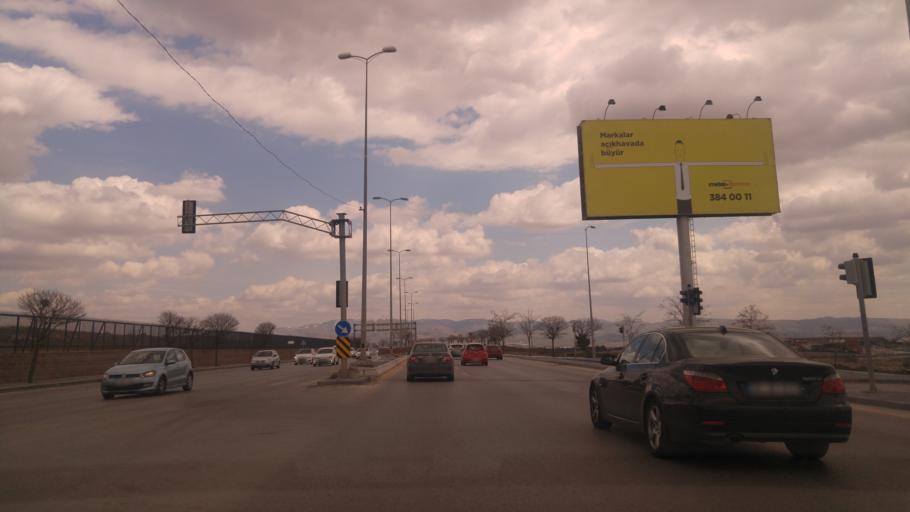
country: TR
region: Ankara
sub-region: Goelbasi
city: Golbasi
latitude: 39.8361
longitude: 32.7648
